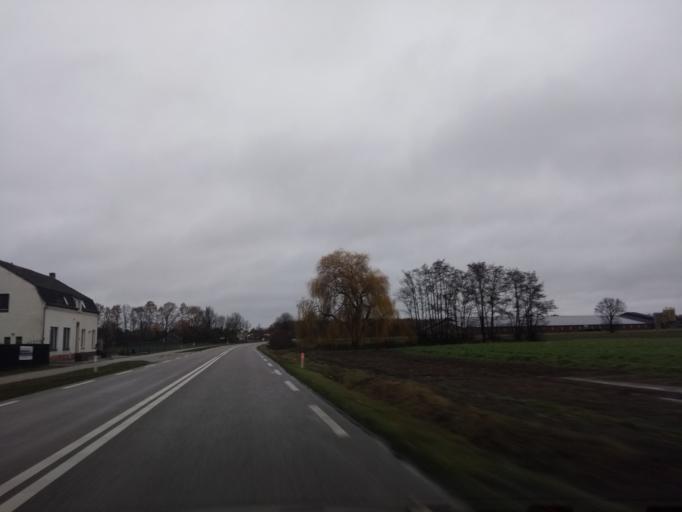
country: NL
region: Limburg
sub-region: Gemeente Weert
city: Weert
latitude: 51.2209
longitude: 5.7195
